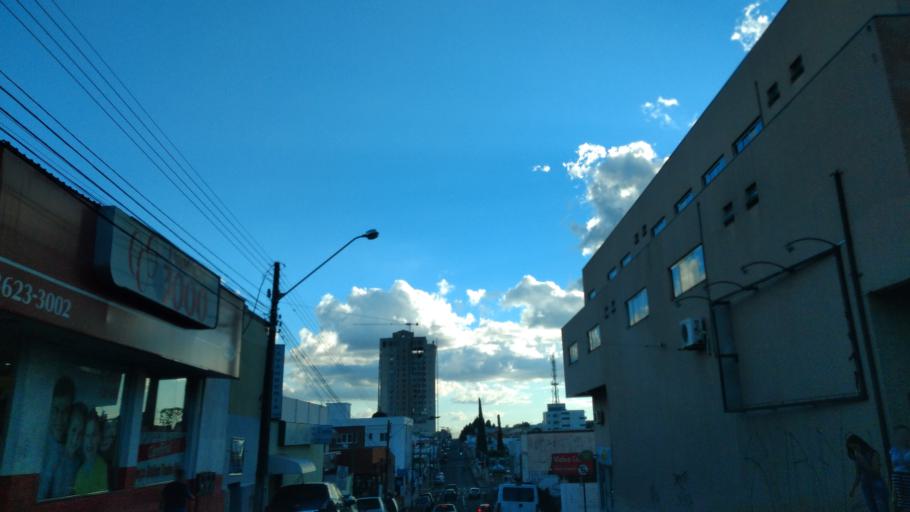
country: BR
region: Parana
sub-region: Guarapuava
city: Guarapuava
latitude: -25.3943
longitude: -51.4702
